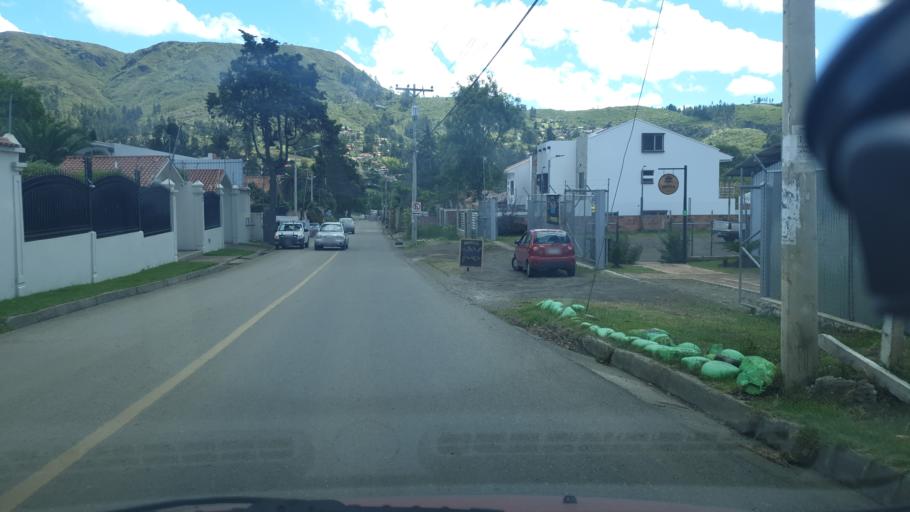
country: EC
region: Azuay
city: Llacao
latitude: -2.8519
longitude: -78.9104
